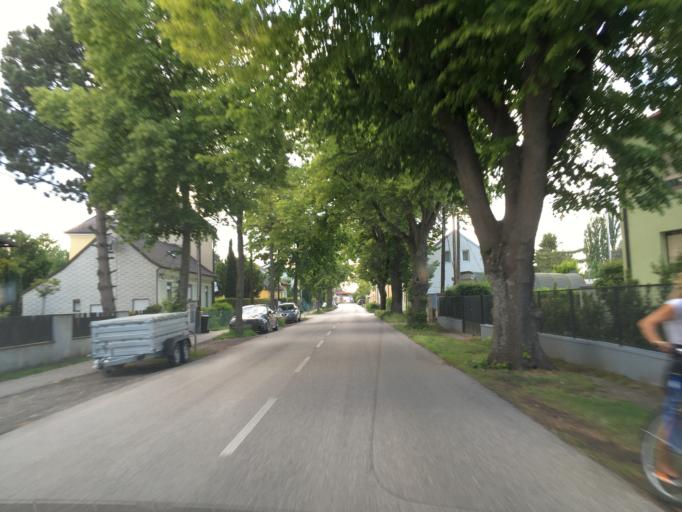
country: AT
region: Lower Austria
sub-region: Politischer Bezirk Wien-Umgebung
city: Gerasdorf bei Wien
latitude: 48.2834
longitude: 16.4868
